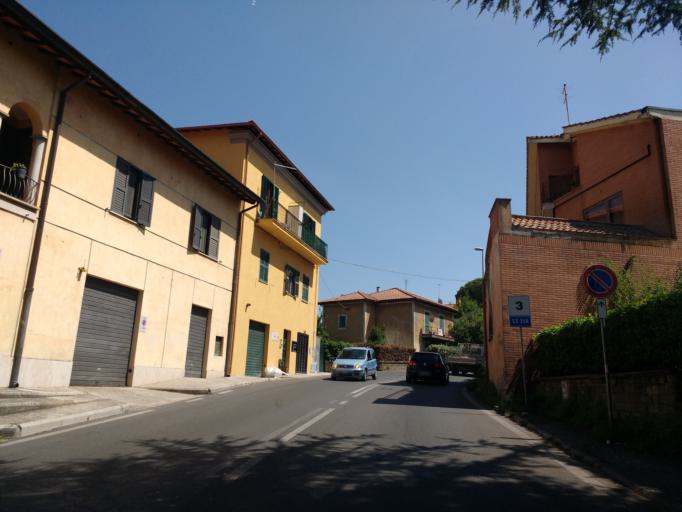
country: IT
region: Latium
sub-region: Citta metropolitana di Roma Capitale
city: Grottaferrata
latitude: 41.7810
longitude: 12.6843
